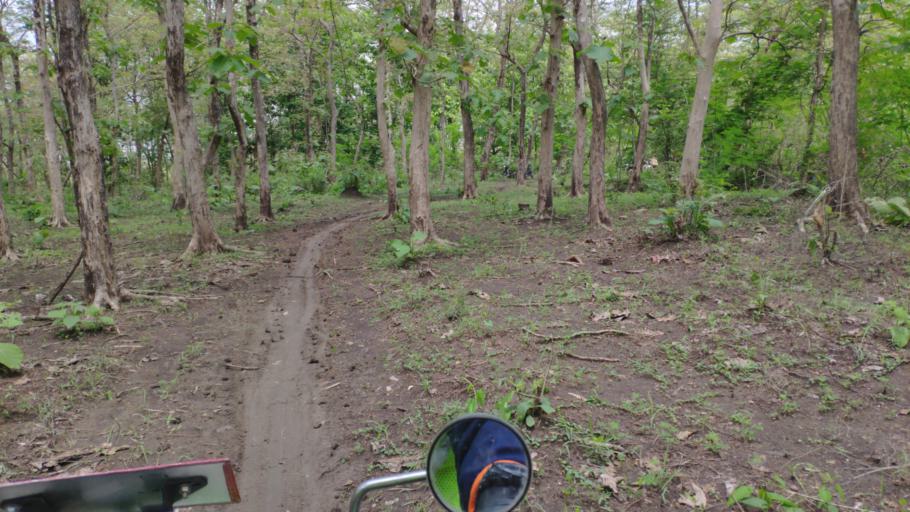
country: ID
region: Central Java
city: Kadengan
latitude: -7.1600
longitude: 111.3014
